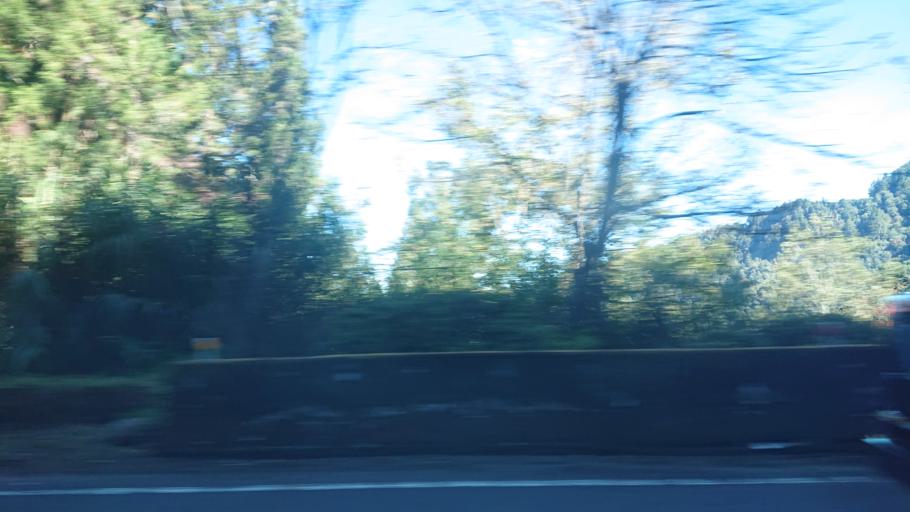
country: TW
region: Taiwan
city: Lugu
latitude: 23.4733
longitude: 120.8448
